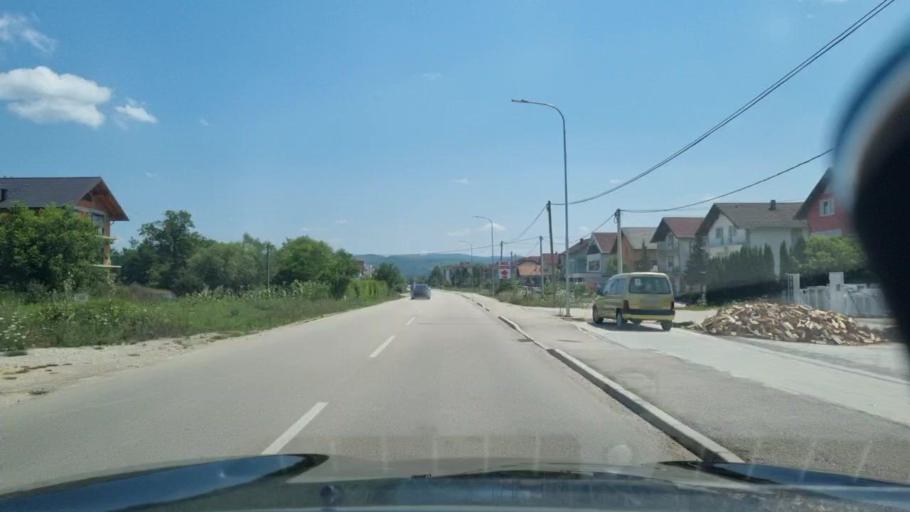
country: BA
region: Federation of Bosnia and Herzegovina
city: Sanski Most
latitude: 44.7711
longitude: 16.6483
